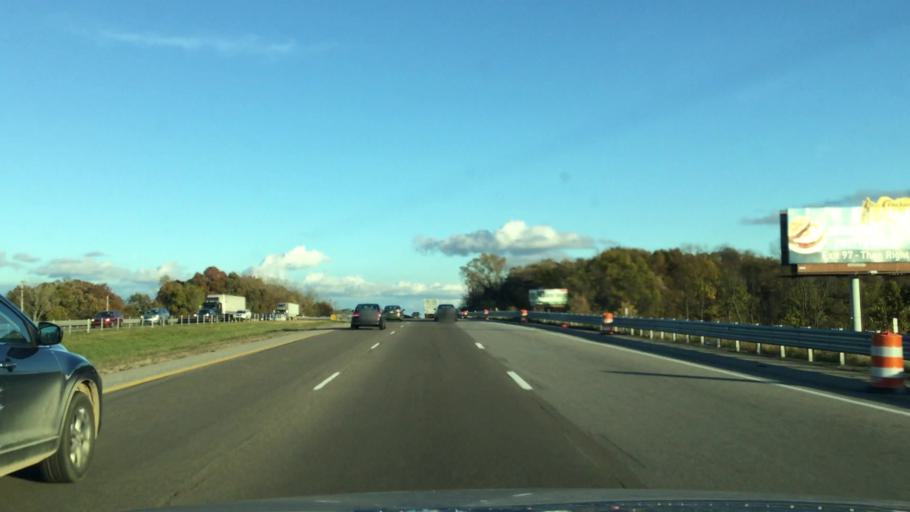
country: US
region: Michigan
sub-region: Calhoun County
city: Springfield
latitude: 42.2712
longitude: -85.2892
